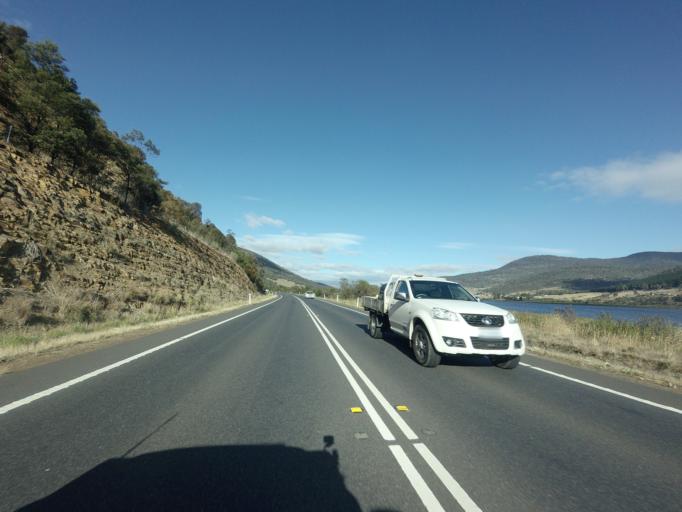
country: AU
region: Tasmania
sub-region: Glenorchy
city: Granton
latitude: -42.7466
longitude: 147.1785
